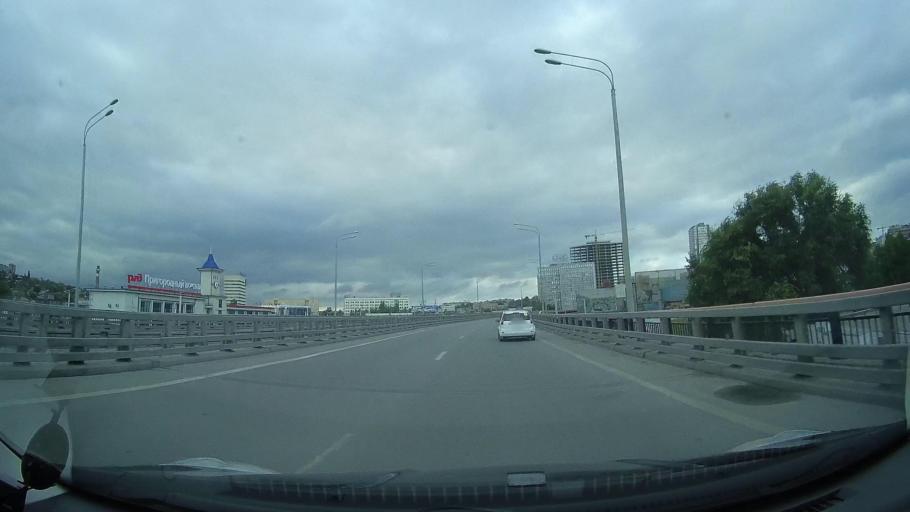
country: RU
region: Rostov
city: Rostov-na-Donu
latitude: 47.2171
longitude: 39.6965
